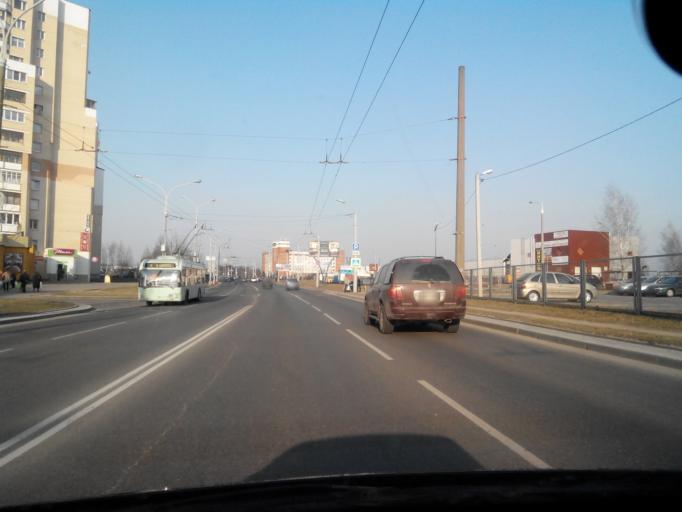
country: BY
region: Minsk
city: Novoye Medvezhino
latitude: 53.8835
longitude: 27.4452
